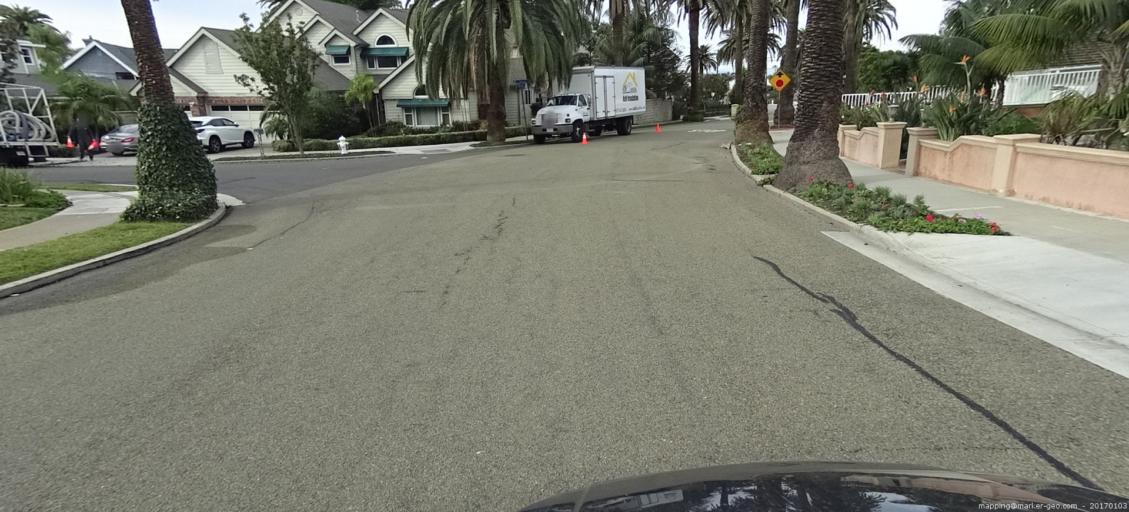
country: US
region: California
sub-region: Orange County
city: Dana Point
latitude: 33.4589
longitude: -117.6667
